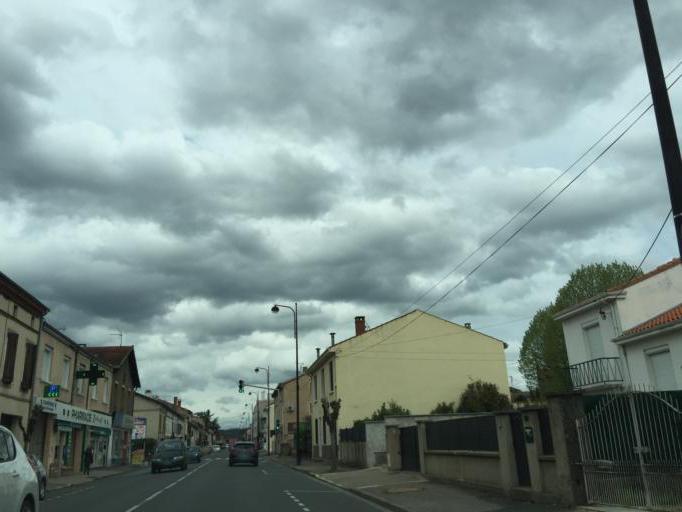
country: FR
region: Midi-Pyrenees
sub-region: Departement du Tarn
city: Albi
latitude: 43.9387
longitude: 2.1478
